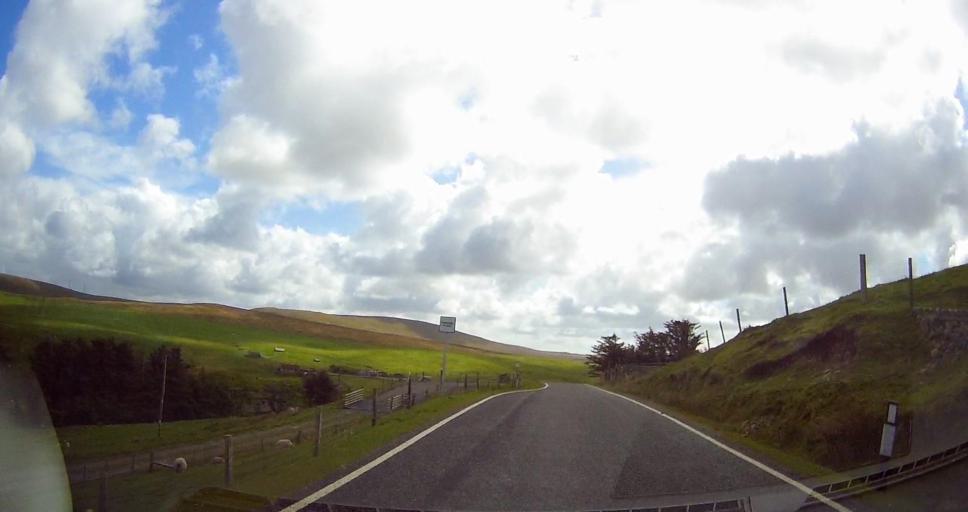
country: GB
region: Scotland
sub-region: Shetland Islands
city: Lerwick
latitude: 60.5293
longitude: -1.3664
